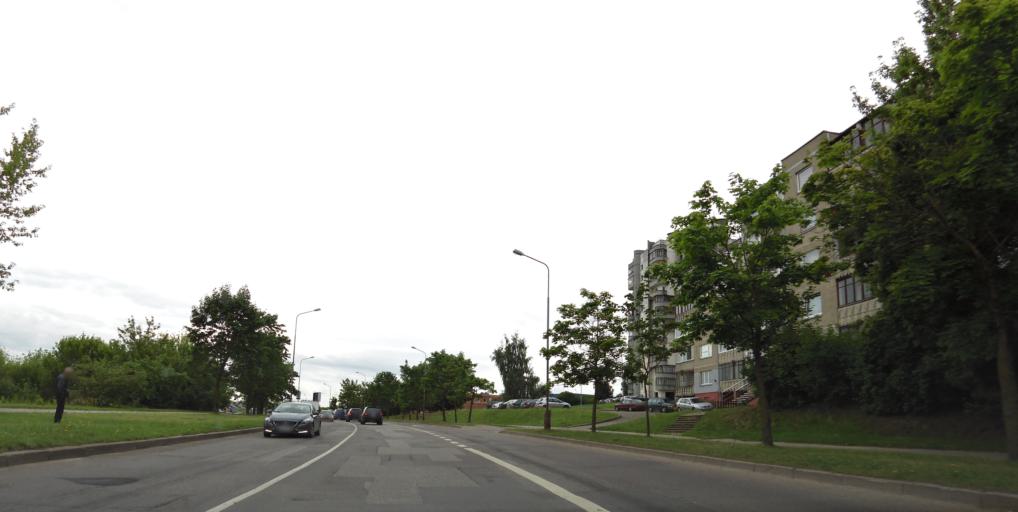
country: LT
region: Vilnius County
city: Seskine
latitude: 54.7129
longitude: 25.2562
